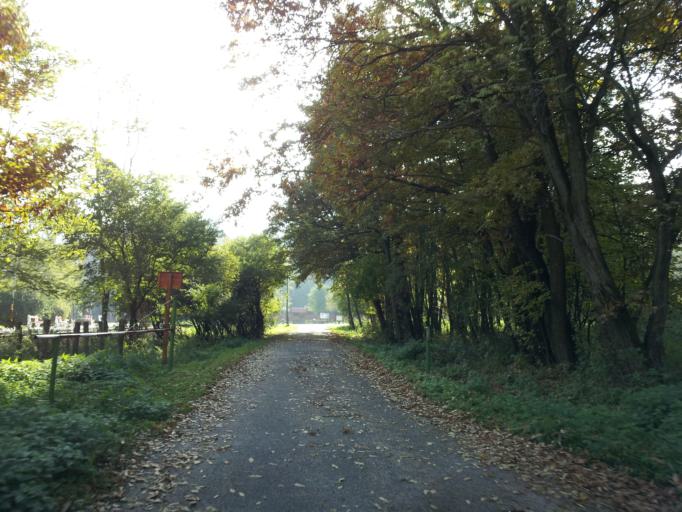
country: HU
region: Gyor-Moson-Sopron
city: Bakonyszentlaszlo
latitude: 47.3607
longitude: 17.8192
